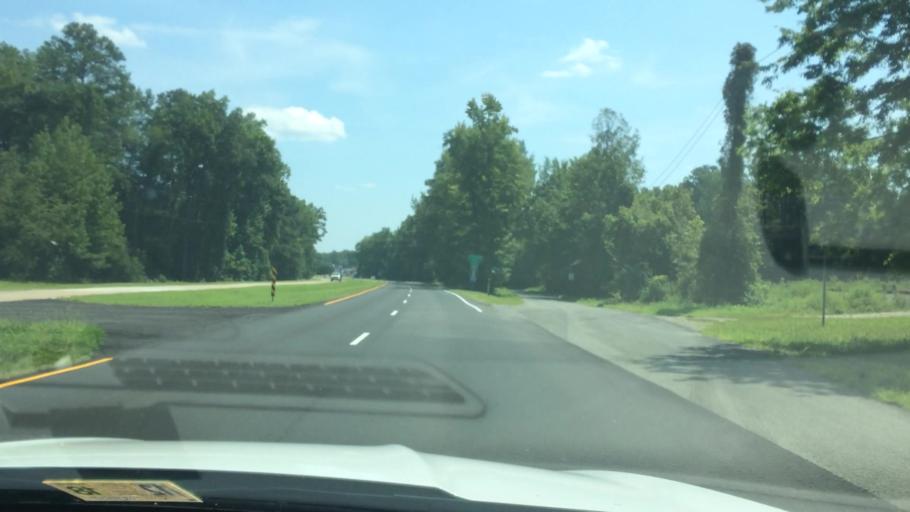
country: US
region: Virginia
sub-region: Charles City County
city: Charles City
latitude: 37.4432
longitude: -77.0508
